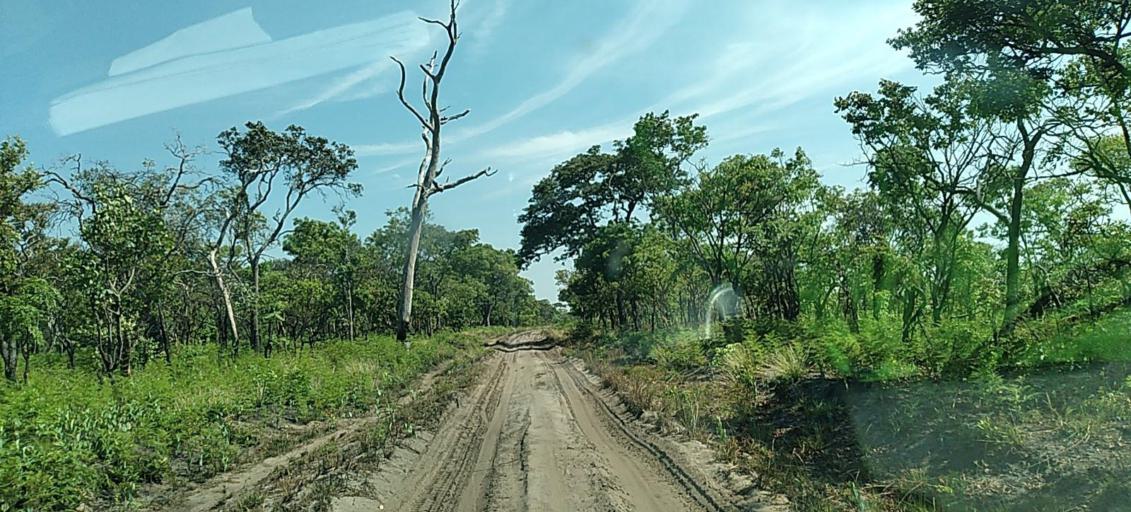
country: ZM
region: North-Western
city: Mwinilunga
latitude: -11.7939
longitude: 25.1674
